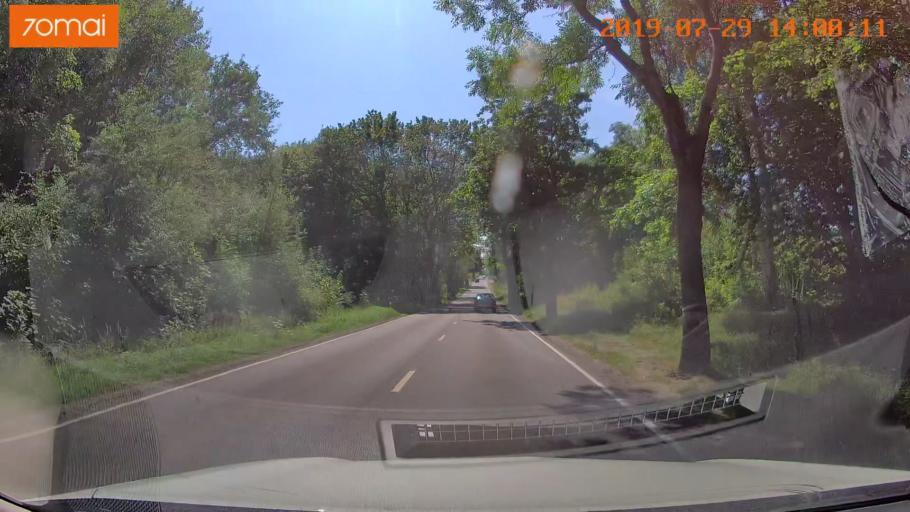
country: RU
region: Kaliningrad
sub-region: Gorod Kaliningrad
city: Baltiysk
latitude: 54.6806
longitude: 19.9294
